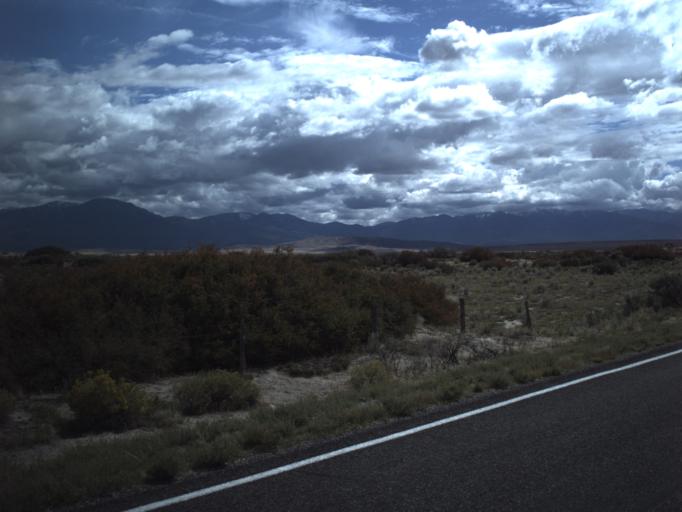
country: US
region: Utah
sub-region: Millard County
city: Fillmore
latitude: 39.1194
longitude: -112.4094
